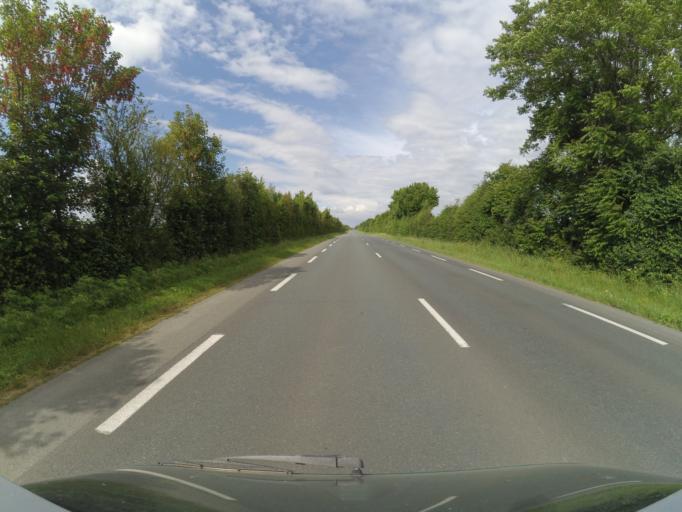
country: FR
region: Pays de la Loire
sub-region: Departement de la Vendee
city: Sainte-Gemme-la-Plaine
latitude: 46.5111
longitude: -1.0927
